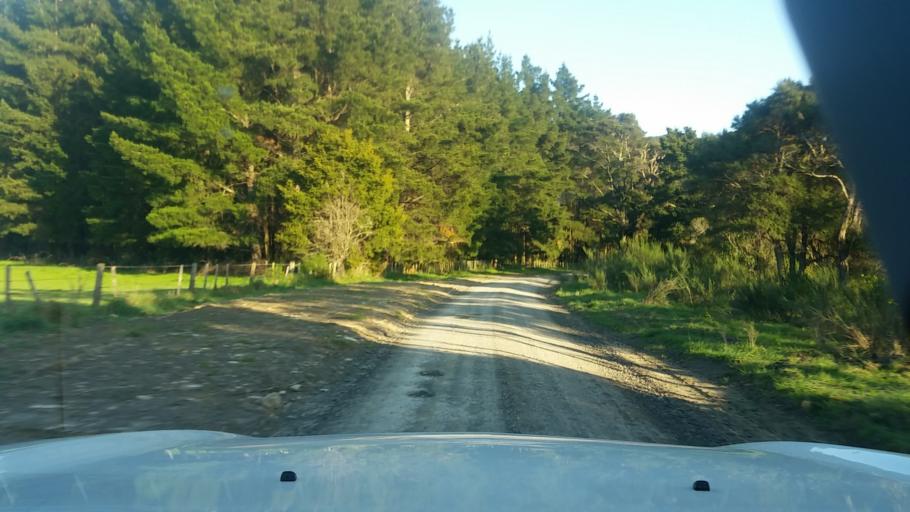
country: NZ
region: Wellington
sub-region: Masterton District
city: Masterton
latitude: -41.0605
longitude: 175.4014
